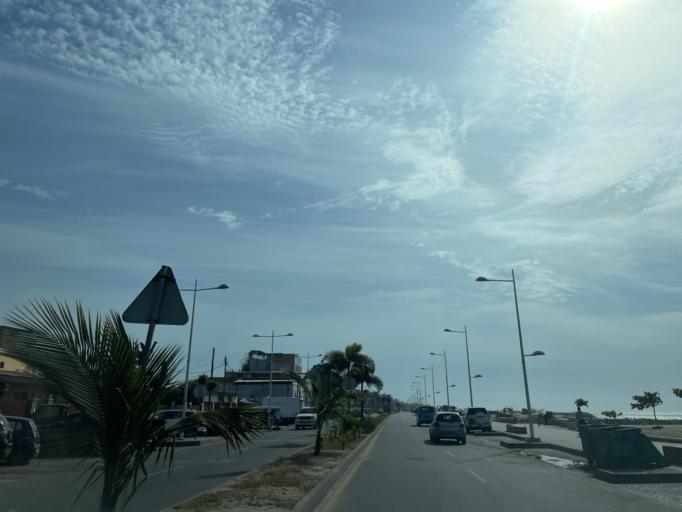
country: AO
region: Luanda
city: Luanda
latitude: -8.7709
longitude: 13.2516
